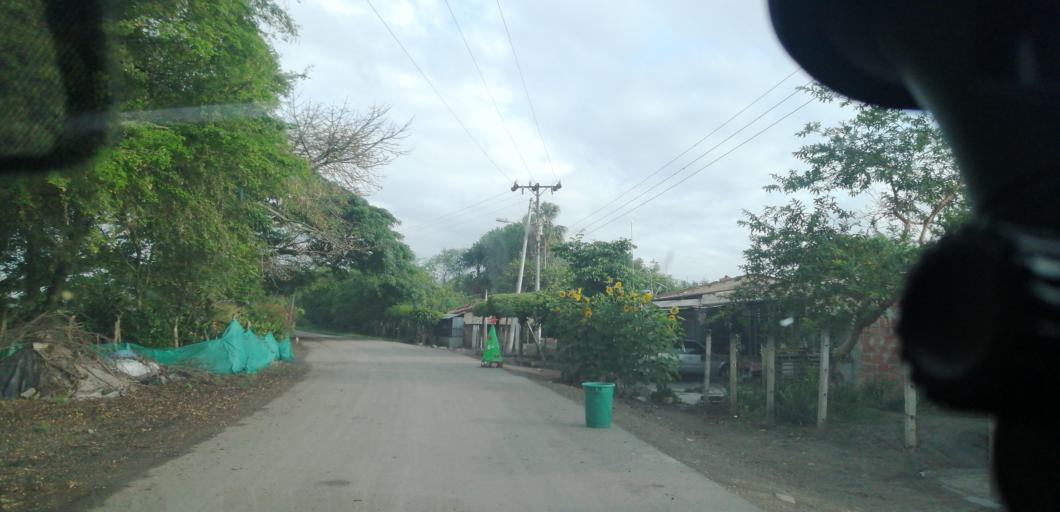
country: CO
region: Valle del Cauca
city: Palmira
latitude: 3.5389
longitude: -76.3593
